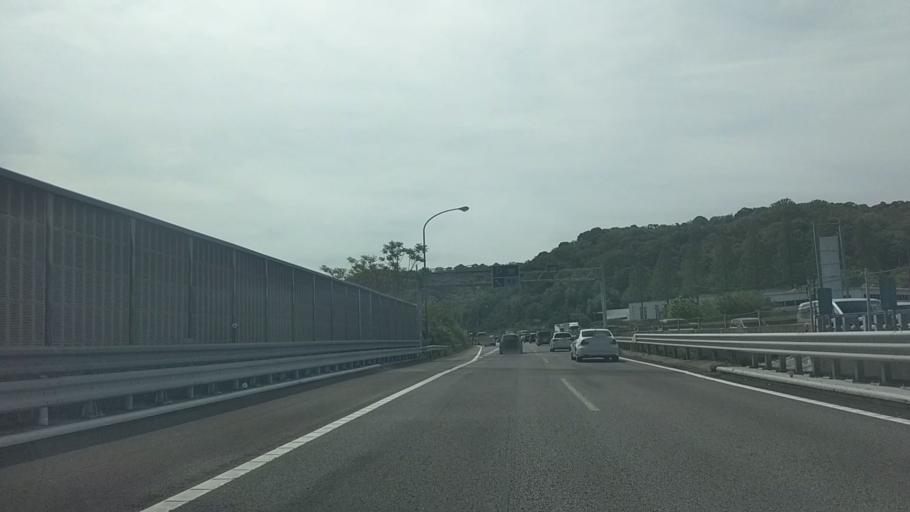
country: JP
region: Aichi
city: Okazaki
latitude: 34.9291
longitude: 137.2225
